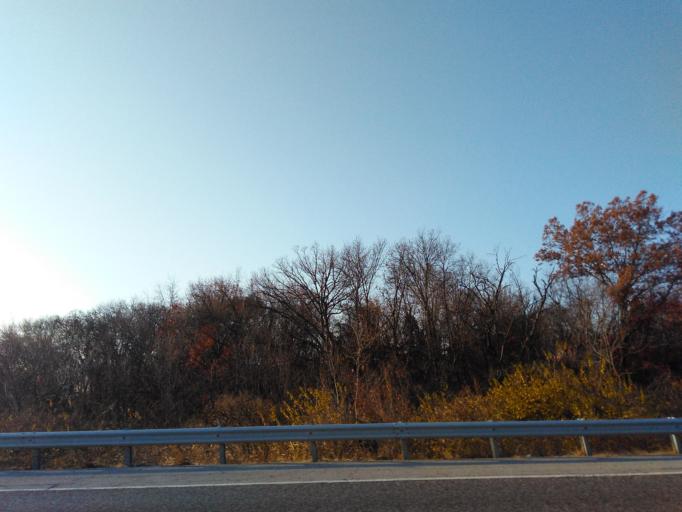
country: US
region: Missouri
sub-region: Saint Louis County
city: Concord
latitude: 38.5072
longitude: -90.3496
